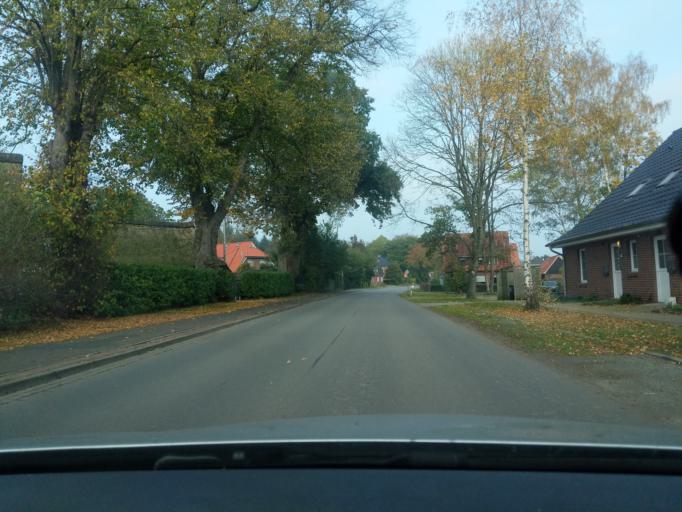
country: DE
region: Lower Saxony
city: Hechthausen
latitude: 53.6320
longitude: 9.2083
